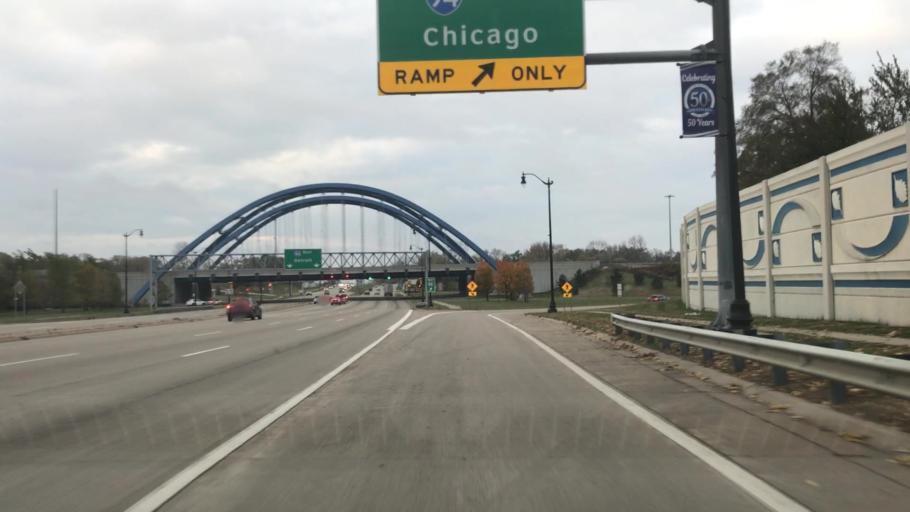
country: US
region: Michigan
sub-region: Wayne County
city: Taylor
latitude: 42.2670
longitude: -83.2706
